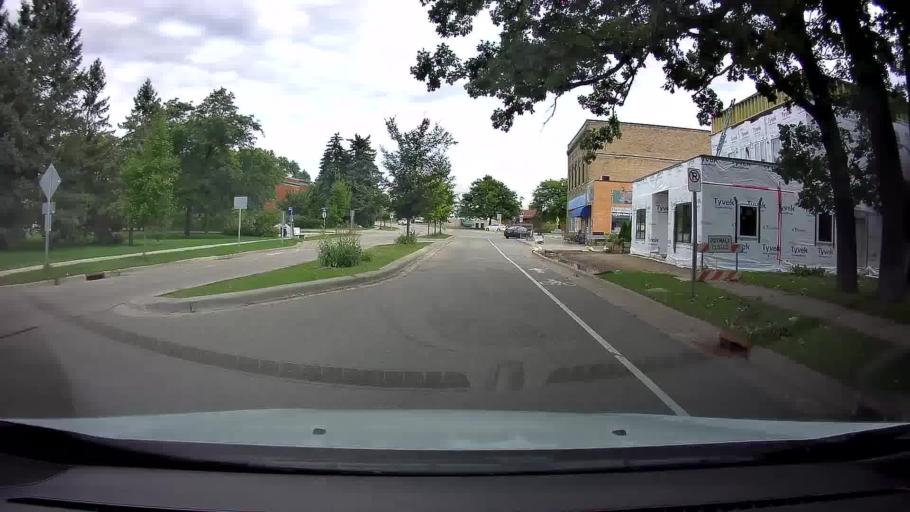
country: US
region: Minnesota
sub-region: Ramsey County
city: Lauderdale
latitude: 44.9688
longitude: -93.1983
